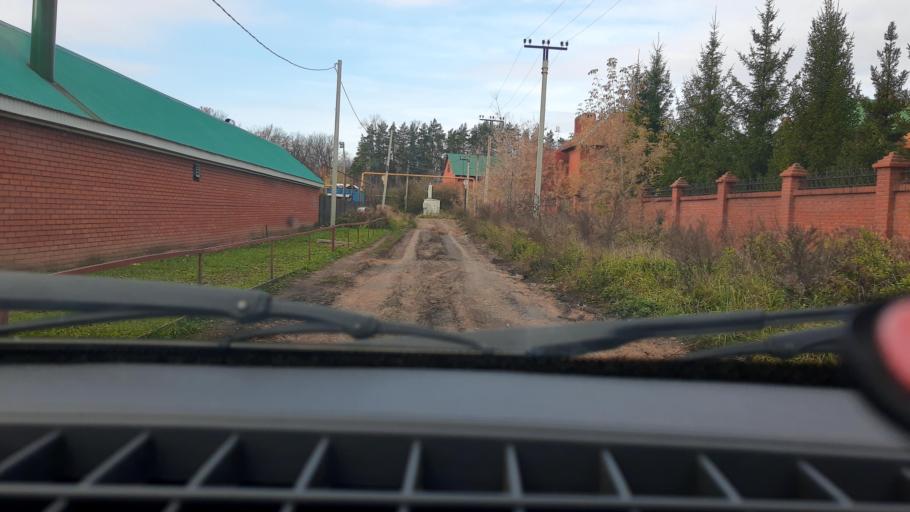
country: RU
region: Bashkortostan
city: Ufa
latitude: 54.7900
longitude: 55.9446
